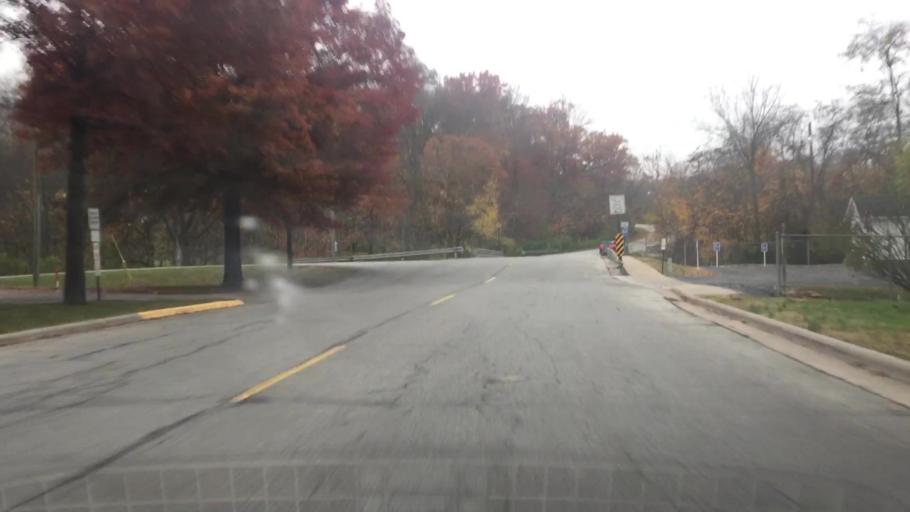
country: US
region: Missouri
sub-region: Callaway County
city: Fulton
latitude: 38.8442
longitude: -91.9540
